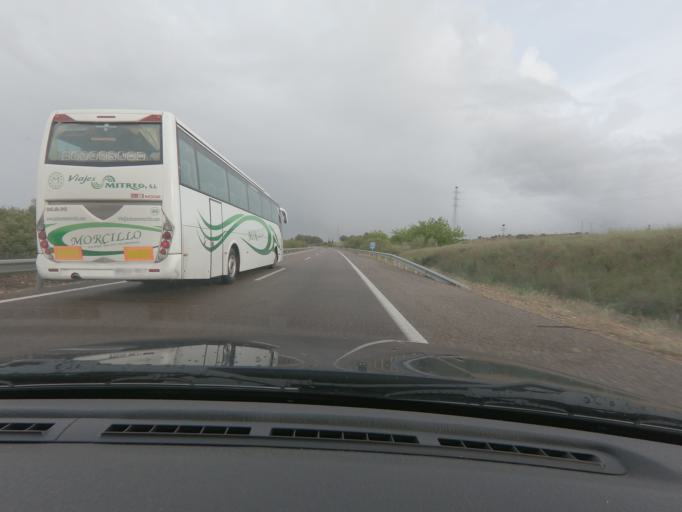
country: ES
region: Extremadura
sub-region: Provincia de Badajoz
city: Badajoz
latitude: 38.8772
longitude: -6.8828
